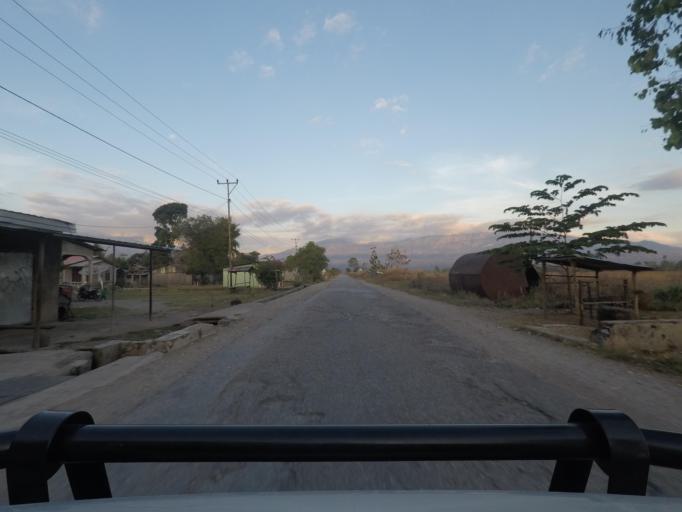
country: TL
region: Bobonaro
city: Maliana
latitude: -8.9767
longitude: 125.1438
